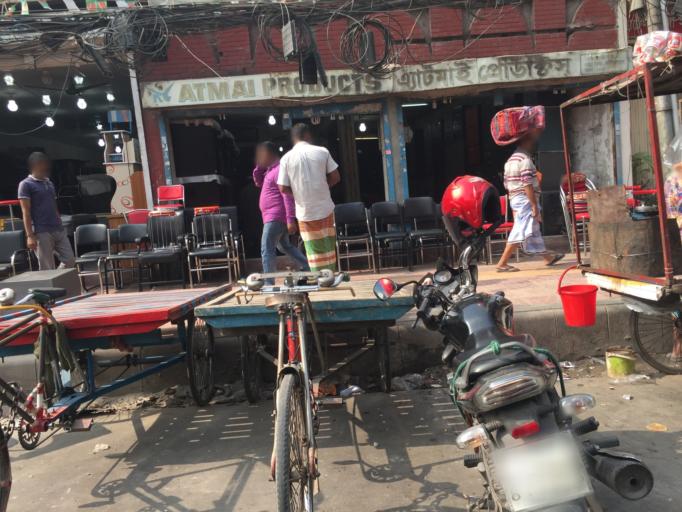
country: BD
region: Dhaka
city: Paltan
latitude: 23.7324
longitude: 90.4152
